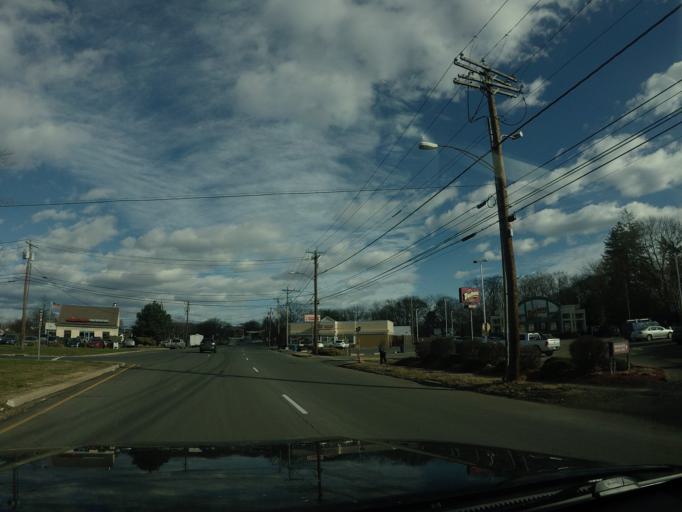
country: US
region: Connecticut
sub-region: Fairfield County
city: Fairfield
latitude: 41.1477
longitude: -73.2455
